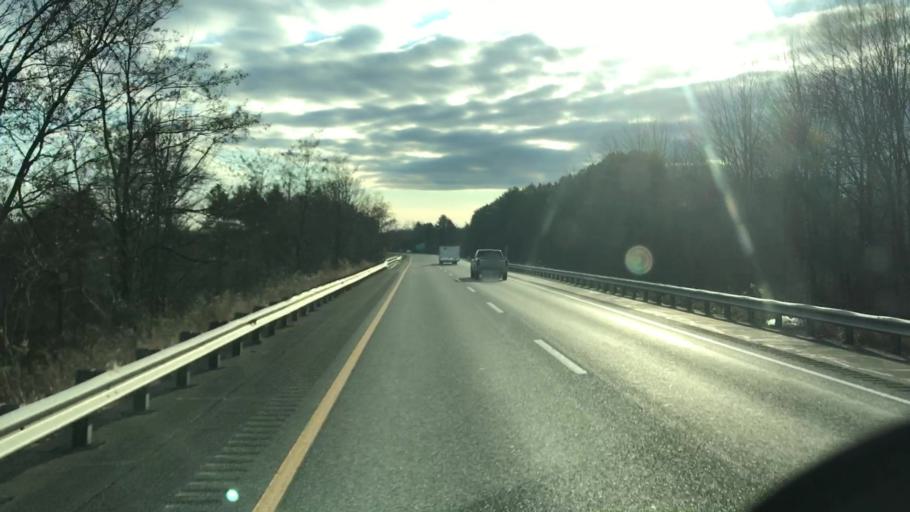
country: US
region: Maine
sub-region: Kennebec County
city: Oakland
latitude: 44.5256
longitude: -69.6958
